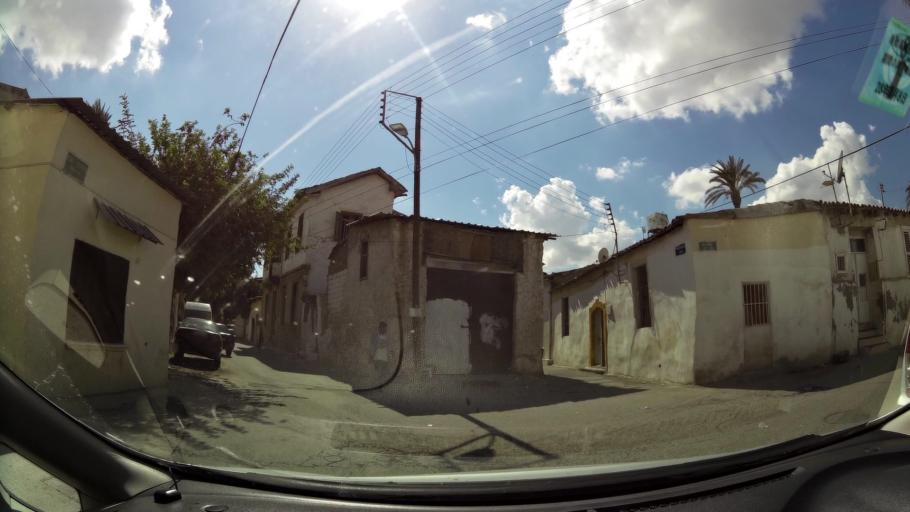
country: CY
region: Lefkosia
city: Nicosia
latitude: 35.1786
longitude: 33.3641
